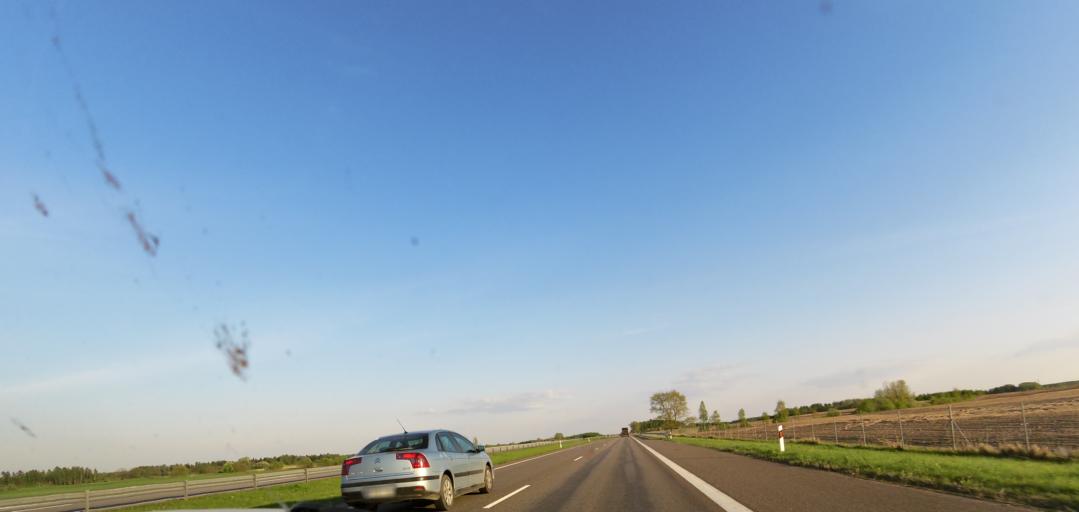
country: LT
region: Vilnius County
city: Ukmerge
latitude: 55.1348
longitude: 24.8338
